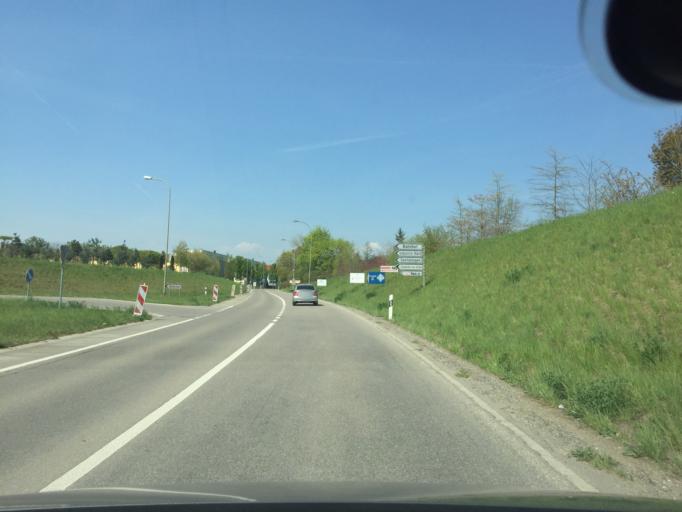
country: CH
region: Zurich
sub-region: Bezirk Buelach
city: Rafz
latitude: 47.6058
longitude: 8.5460
